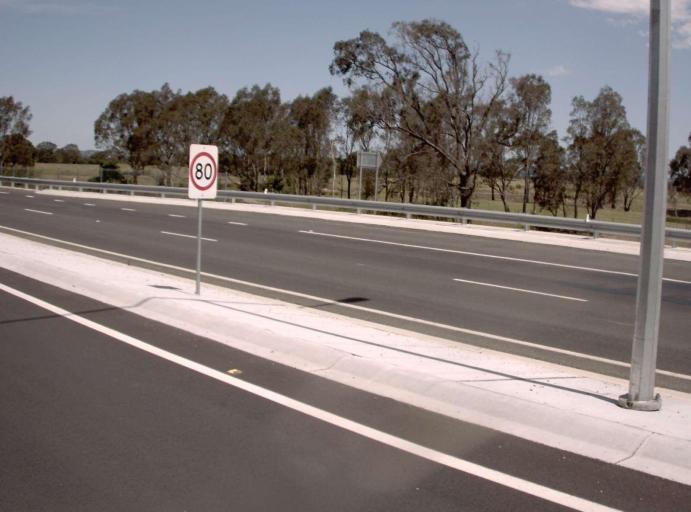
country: AU
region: Victoria
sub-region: Wellington
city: Sale
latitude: -38.1120
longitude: 147.0435
